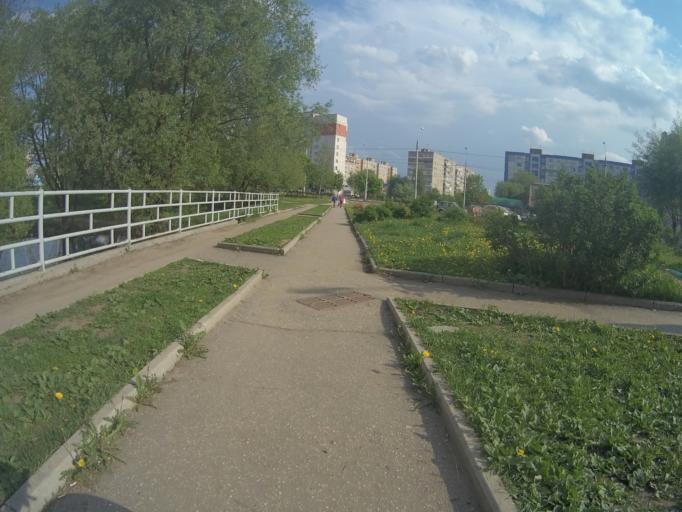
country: RU
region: Vladimir
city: Kommunar
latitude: 56.1656
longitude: 40.4509
